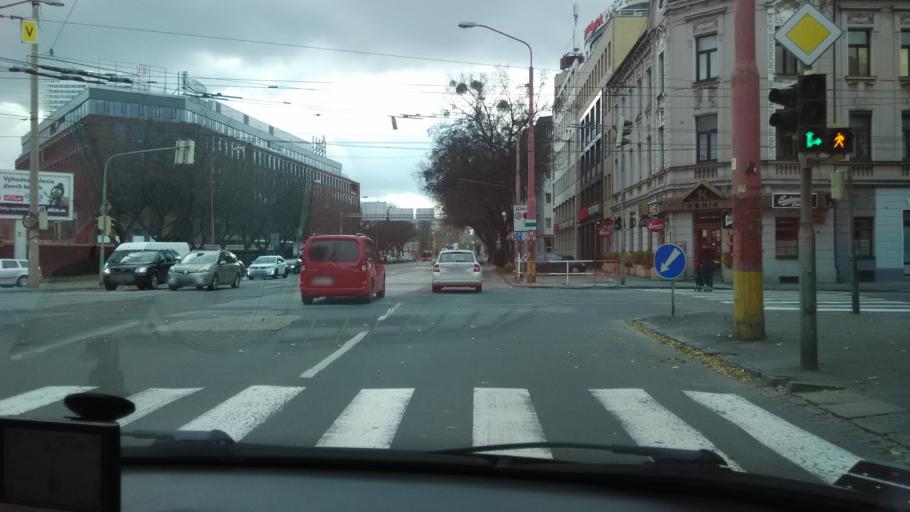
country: SK
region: Bratislavsky
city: Bratislava
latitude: 48.1468
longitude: 17.1240
